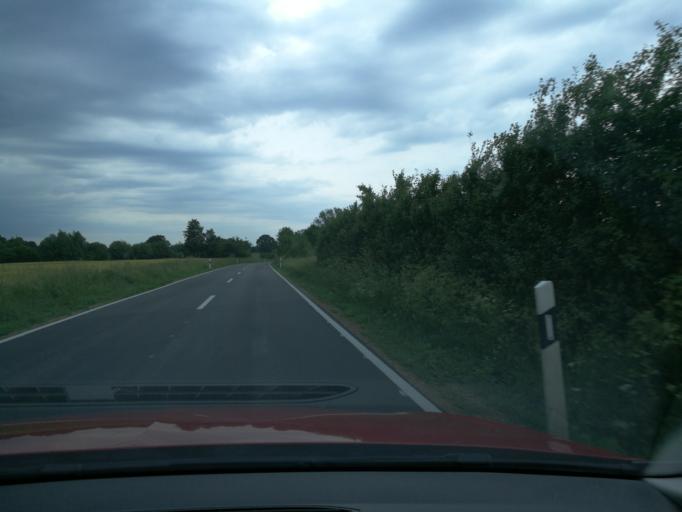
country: DE
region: Schleswig-Holstein
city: Lasbek
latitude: 53.7311
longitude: 10.3618
